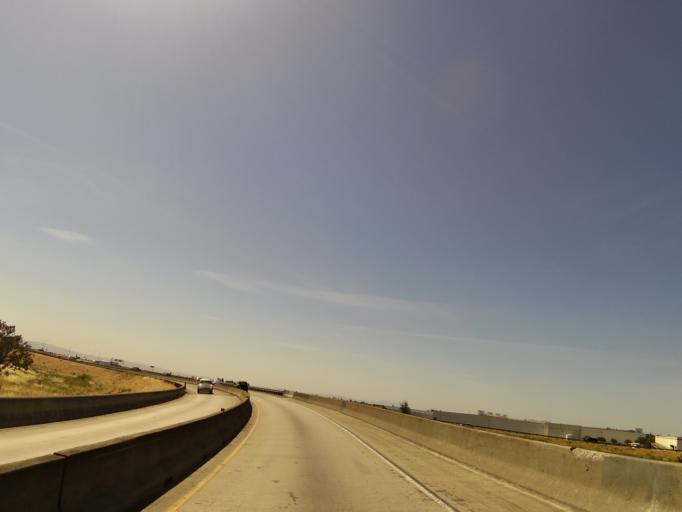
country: US
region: California
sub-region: San Joaquin County
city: Manteca
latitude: 37.7854
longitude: -121.1877
